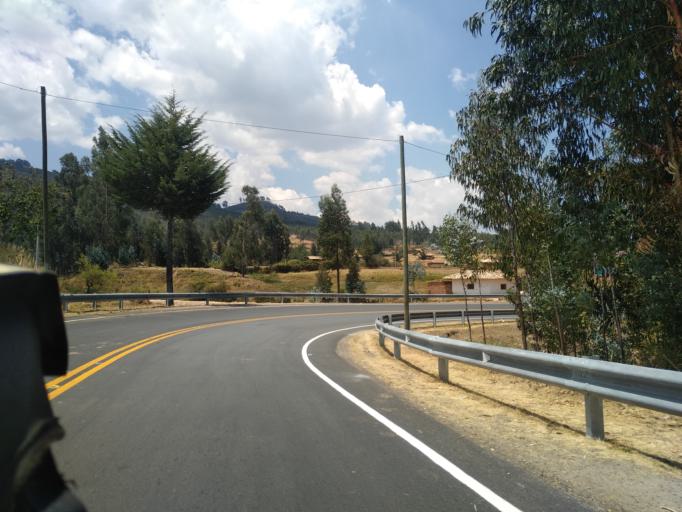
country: PE
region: Cajamarca
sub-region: San Marcos
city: San Marcos
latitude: -7.2911
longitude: -78.2053
